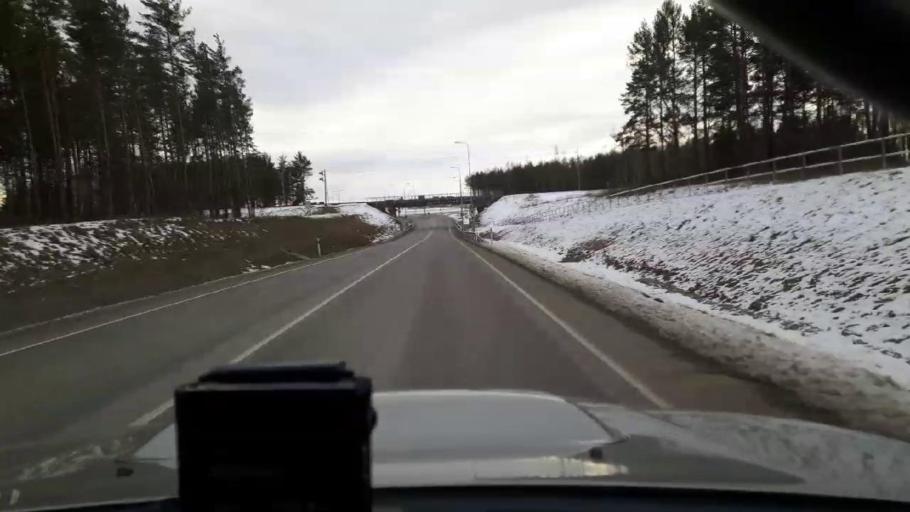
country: EE
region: Harju
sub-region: Saue vald
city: Laagri
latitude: 59.3427
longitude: 24.6052
